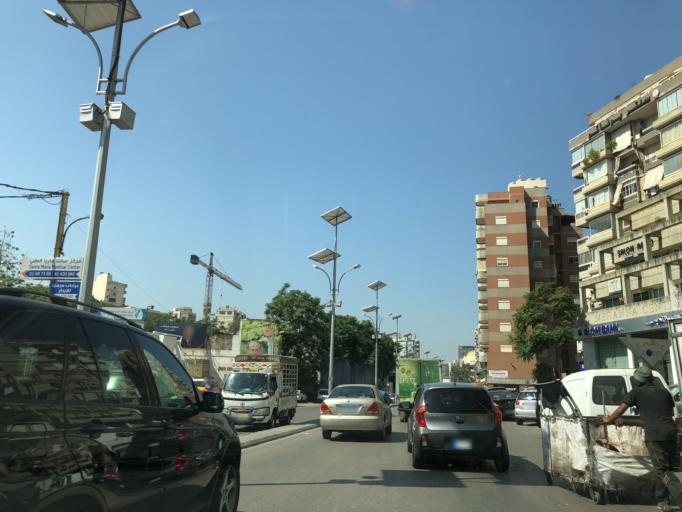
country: LB
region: Mont-Liban
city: Jdaidet el Matn
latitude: 33.8752
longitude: 35.5475
